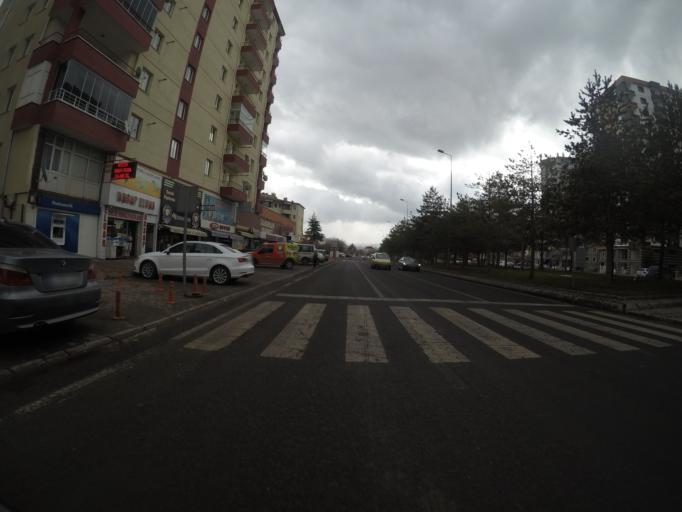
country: TR
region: Kayseri
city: Melikgazi
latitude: 38.7522
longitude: 35.4701
